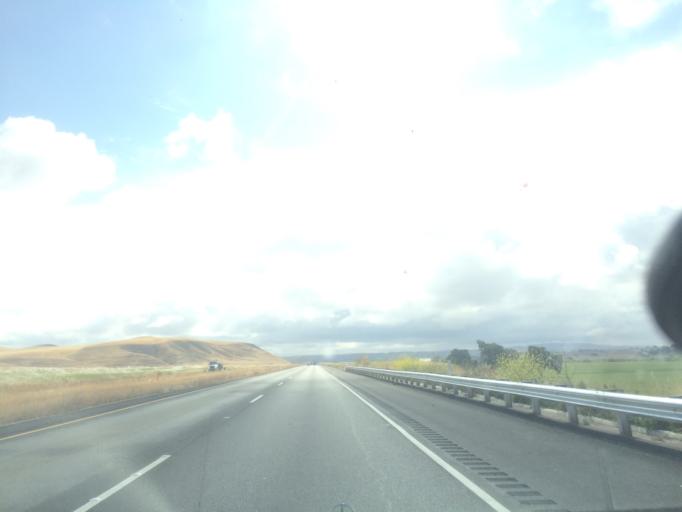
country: US
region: California
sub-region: San Luis Obispo County
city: Shandon
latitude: 35.6598
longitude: -120.4630
